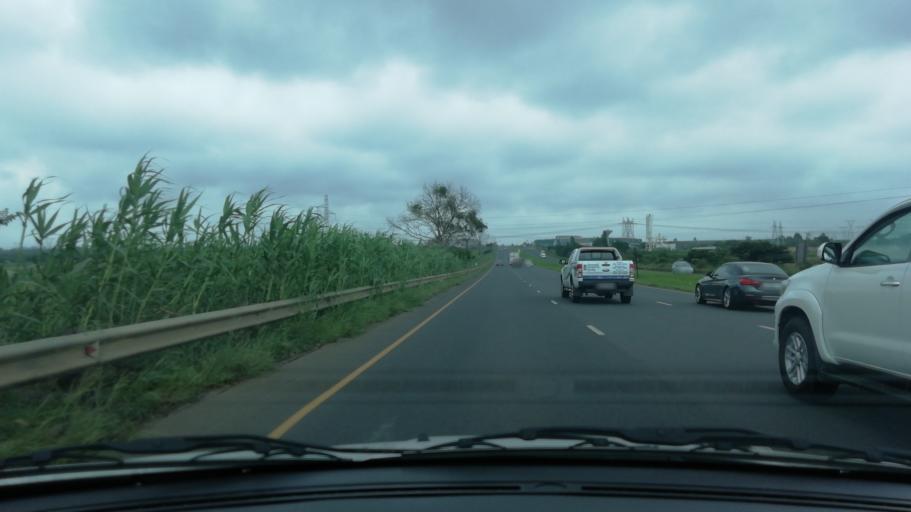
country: ZA
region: KwaZulu-Natal
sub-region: uThungulu District Municipality
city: Empangeni
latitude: -28.7722
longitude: 31.9444
